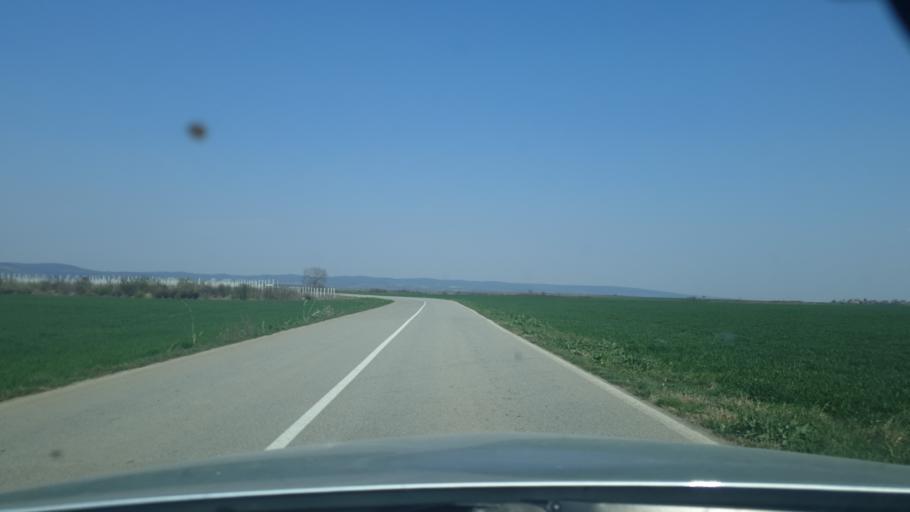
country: RS
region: Autonomna Pokrajina Vojvodina
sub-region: Sremski Okrug
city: Ruma
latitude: 45.0484
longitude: 19.7639
